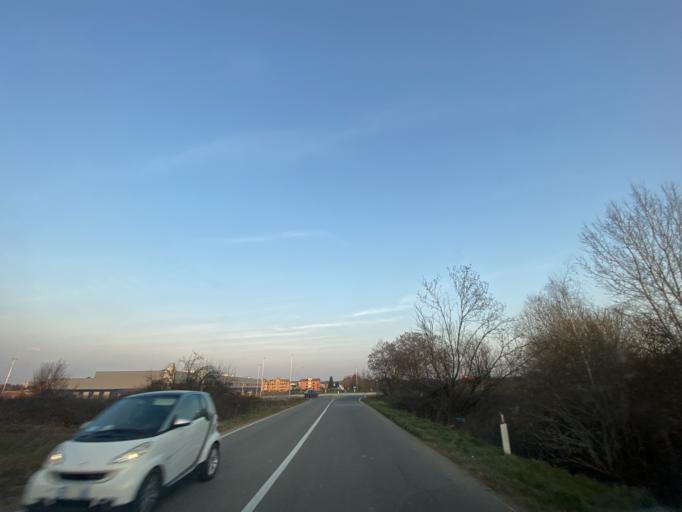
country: IT
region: Lombardy
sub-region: Citta metropolitana di Milano
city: Cesate
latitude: 45.6022
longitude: 9.0726
